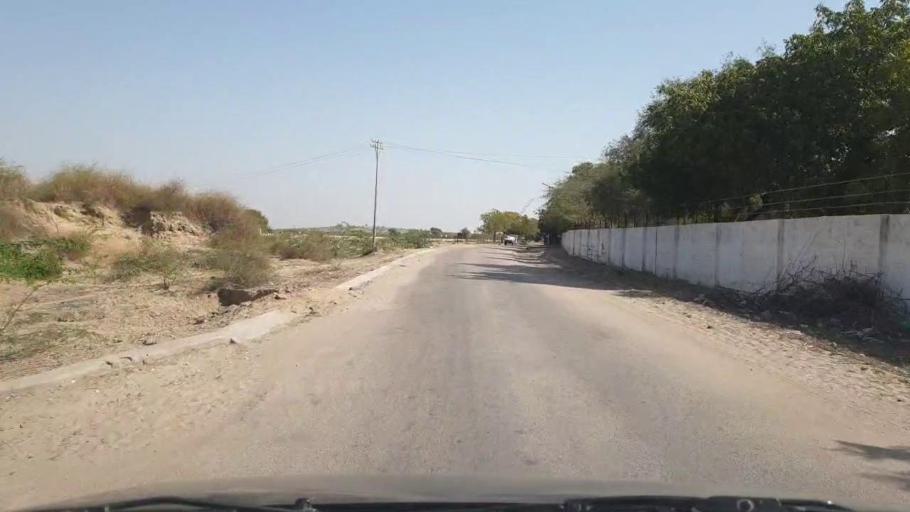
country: PK
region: Sindh
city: Chor
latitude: 25.5262
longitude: 69.8284
